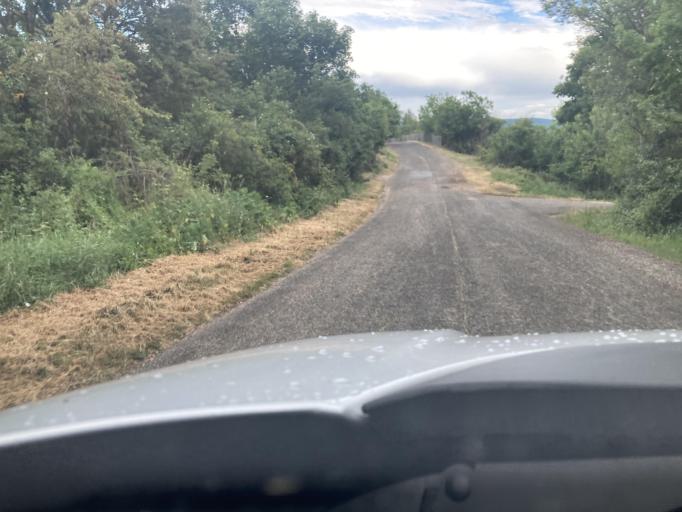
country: IT
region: Abruzzo
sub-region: Provincia dell' Aquila
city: Fossa
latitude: 42.2825
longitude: 13.4920
